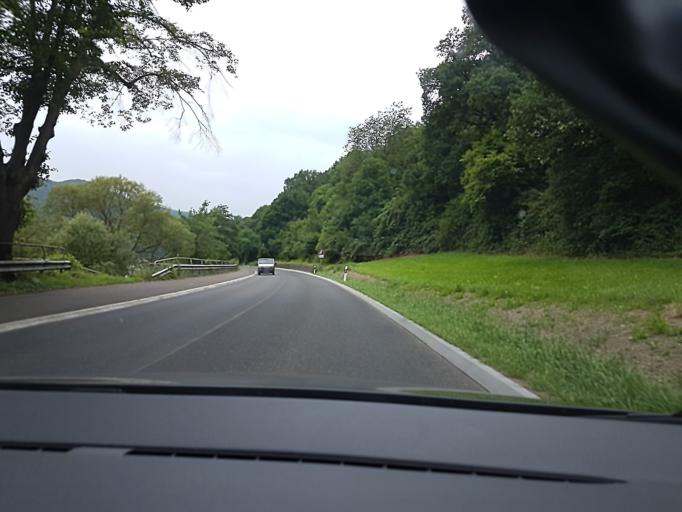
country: DE
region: Rheinland-Pfalz
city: Dausenau
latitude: 50.3271
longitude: 7.7510
